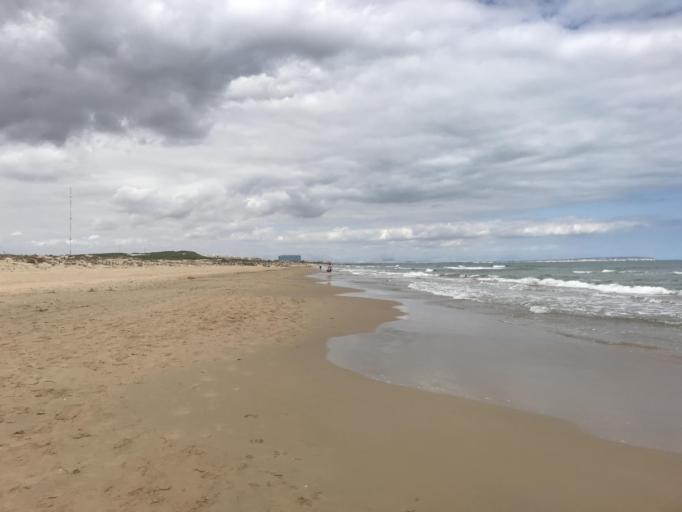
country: ES
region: Valencia
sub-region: Provincia de Alicante
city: Guardamar del Segura
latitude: 38.0438
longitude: -0.6514
